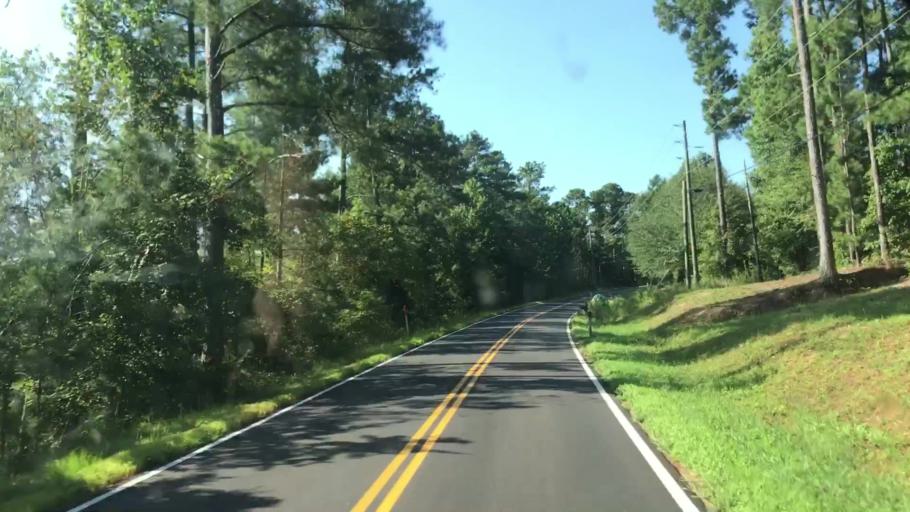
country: US
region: Georgia
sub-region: Walton County
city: Monroe
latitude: 33.8365
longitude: -83.7910
